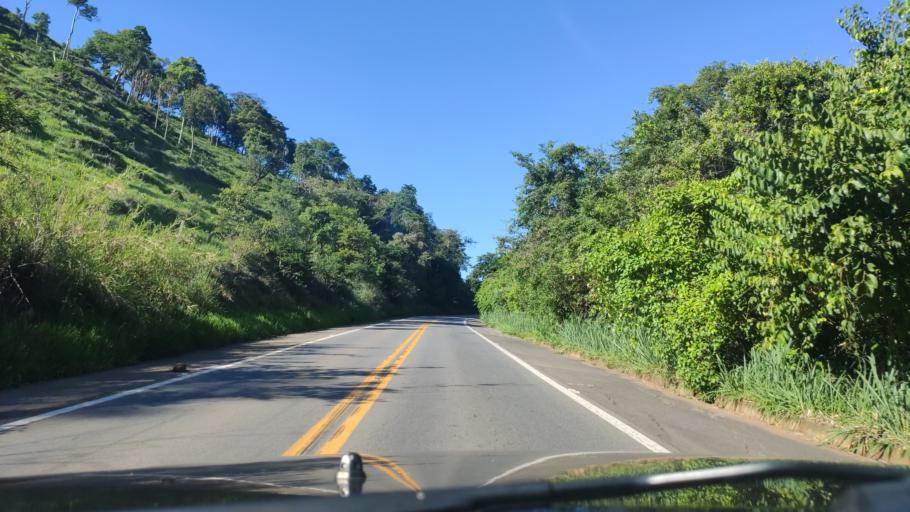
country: BR
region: Sao Paulo
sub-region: Socorro
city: Socorro
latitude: -22.5514
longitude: -46.5803
